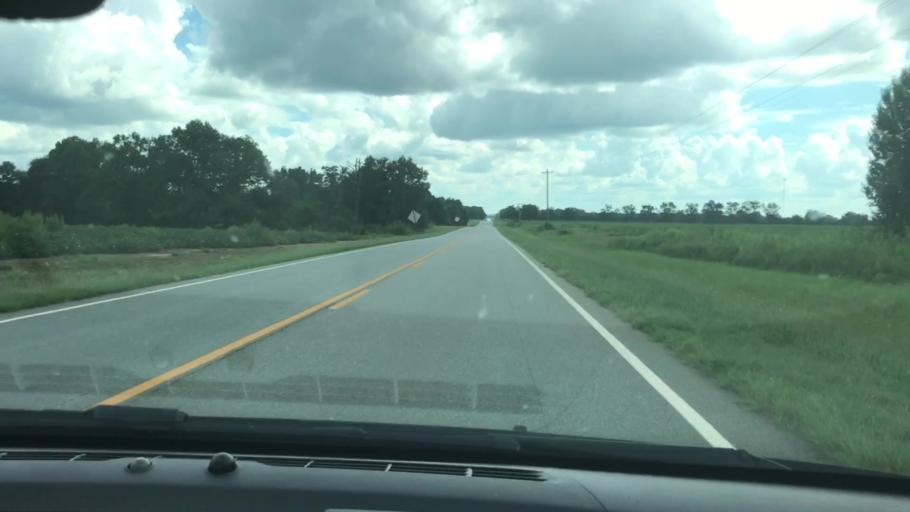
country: US
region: Georgia
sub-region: Quitman County
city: Georgetown
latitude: 31.8127
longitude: -85.0935
